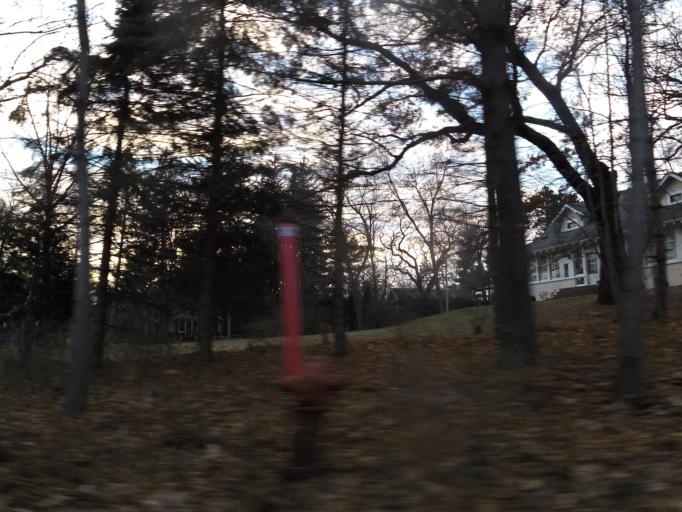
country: US
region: Minnesota
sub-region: Washington County
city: Mahtomedi
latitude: 45.0710
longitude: -92.9555
